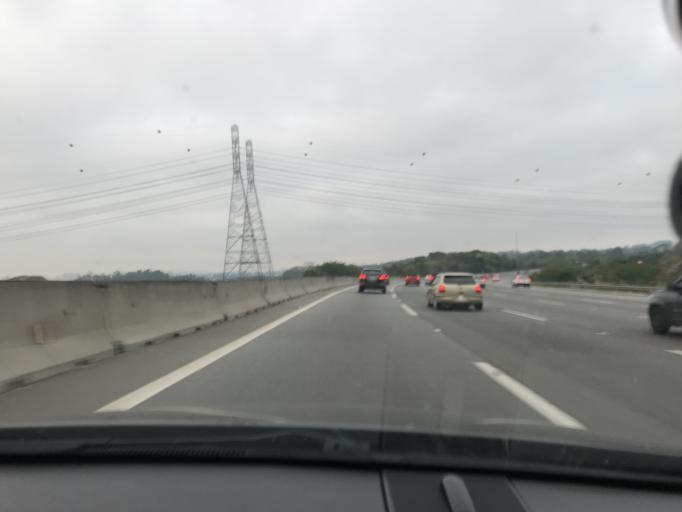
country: BR
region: Sao Paulo
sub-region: Guarulhos
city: Guarulhos
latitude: -23.4980
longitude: -46.5361
